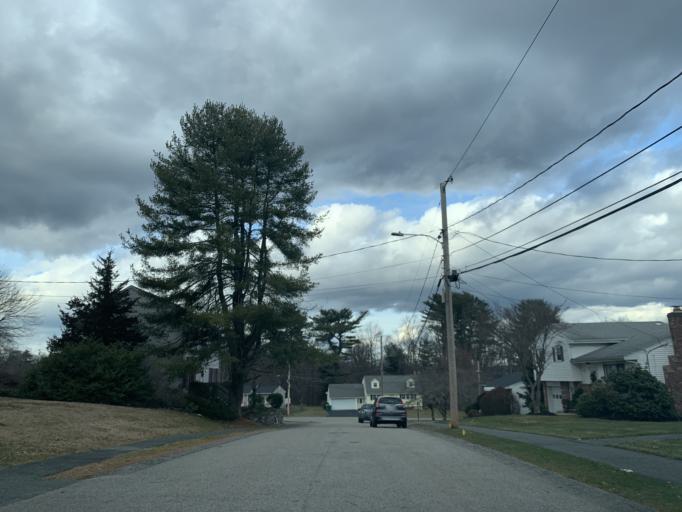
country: US
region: Massachusetts
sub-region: Norfolk County
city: Norwood
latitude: 42.1798
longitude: -71.1751
